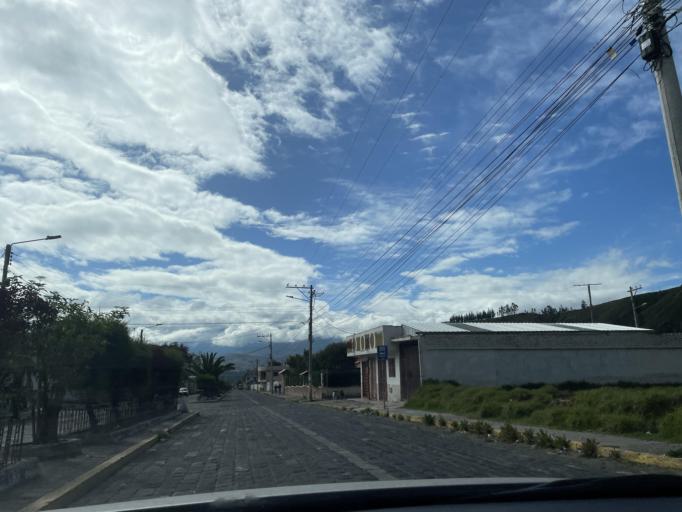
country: EC
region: Chimborazo
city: Guano
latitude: -1.6083
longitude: -78.6393
